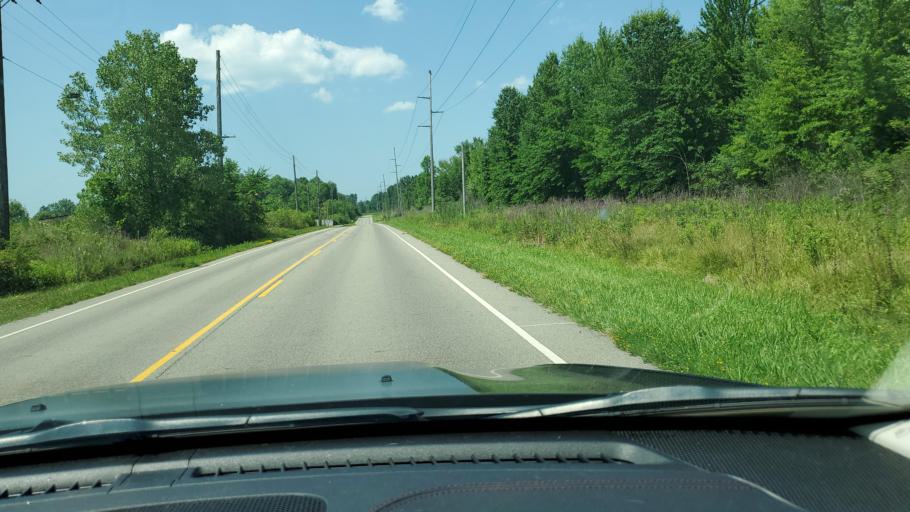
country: US
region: Ohio
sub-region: Trumbull County
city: Bolindale
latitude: 41.1957
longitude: -80.7895
